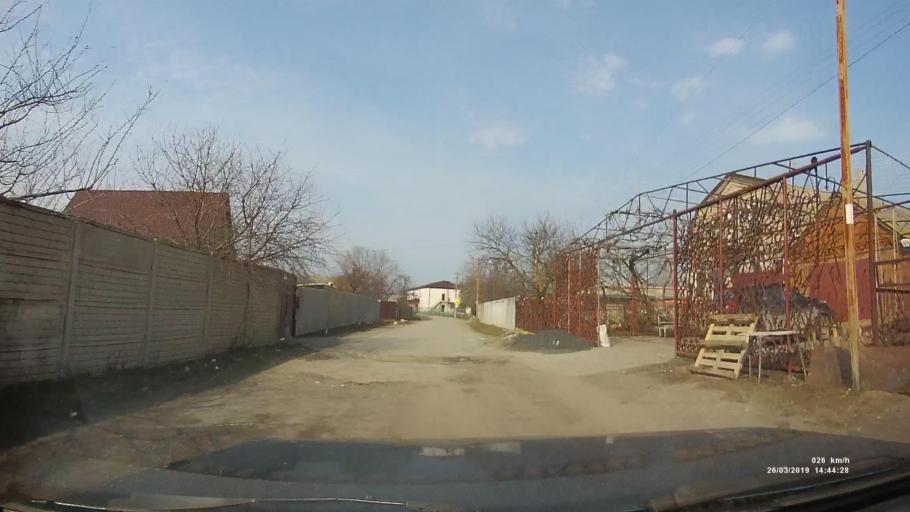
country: RU
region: Rostov
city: Novobessergenovka
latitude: 47.1778
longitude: 38.8627
